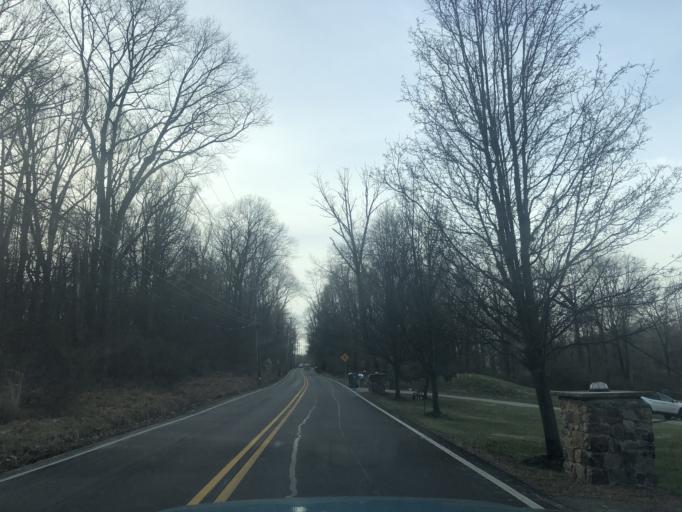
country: US
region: Pennsylvania
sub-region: Montgomery County
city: Flourtown
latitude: 40.1214
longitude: -75.2388
